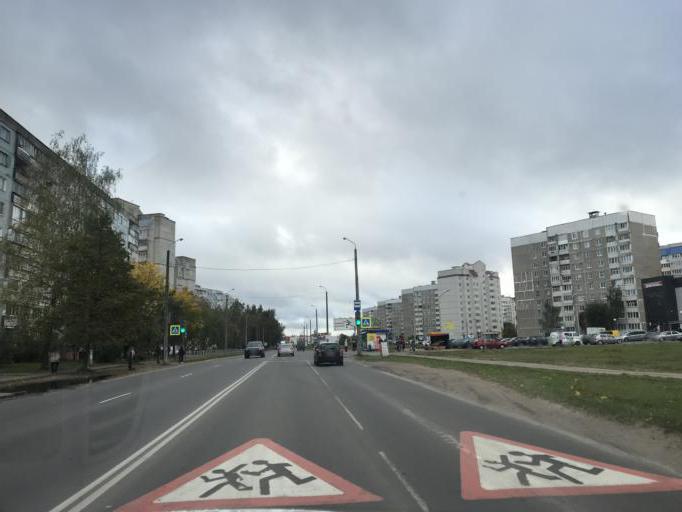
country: BY
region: Mogilev
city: Mahilyow
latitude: 53.8776
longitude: 30.3678
